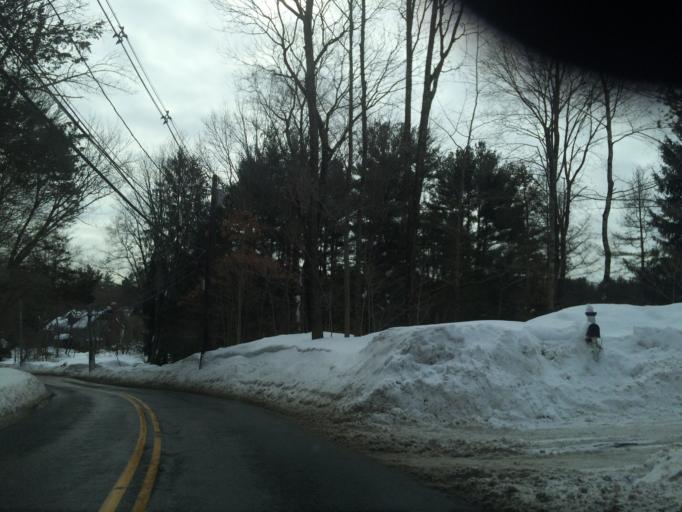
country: US
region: Massachusetts
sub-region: Middlesex County
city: Weston
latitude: 42.3808
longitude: -71.3206
